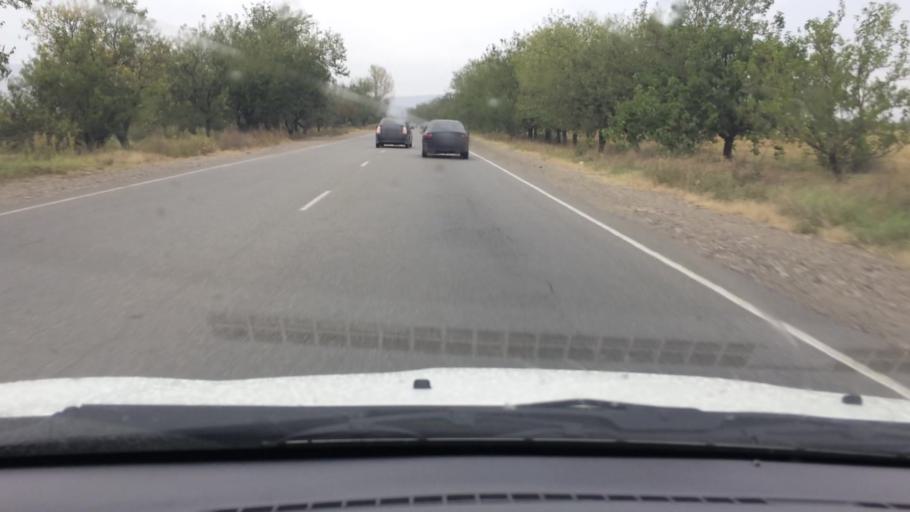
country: GE
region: Kvemo Kartli
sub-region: Marneuli
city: Marneuli
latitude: 41.5647
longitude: 44.7756
